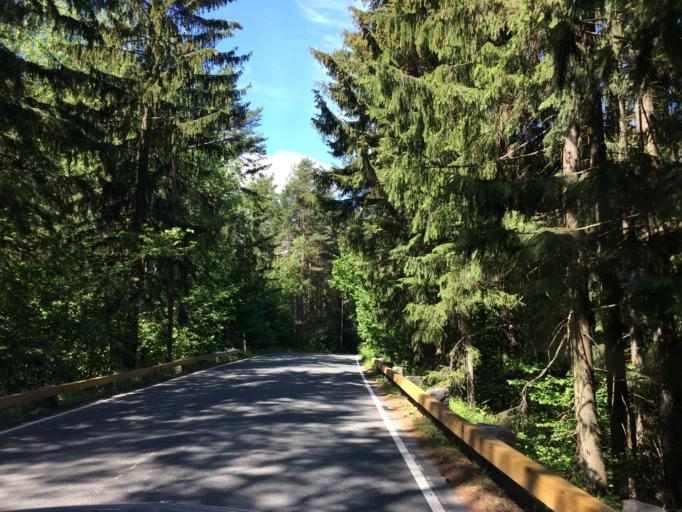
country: FI
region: Haeme
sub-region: Haemeenlinna
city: Haemeenlinna
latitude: 60.9775
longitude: 24.4547
